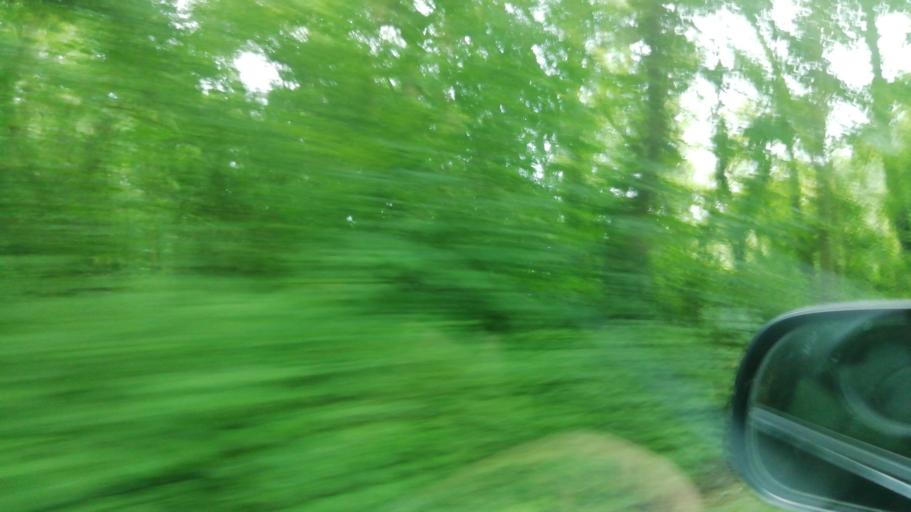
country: IE
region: Munster
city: Fethard
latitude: 52.5098
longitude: -7.6855
